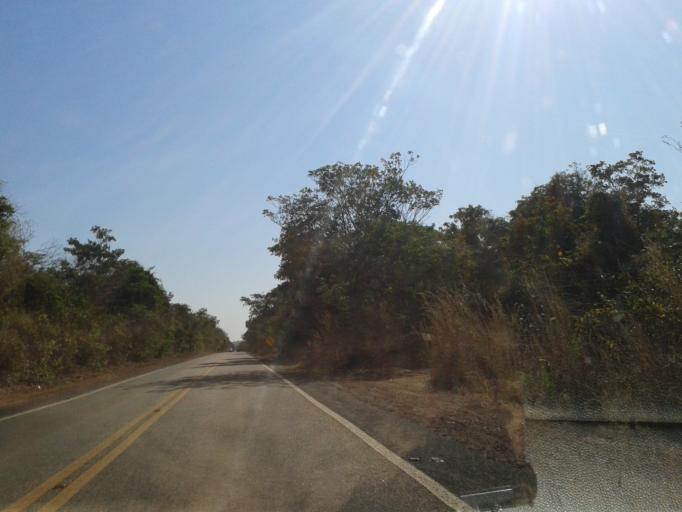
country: BR
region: Goias
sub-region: Mozarlandia
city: Mozarlandia
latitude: -14.6789
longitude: -50.5378
